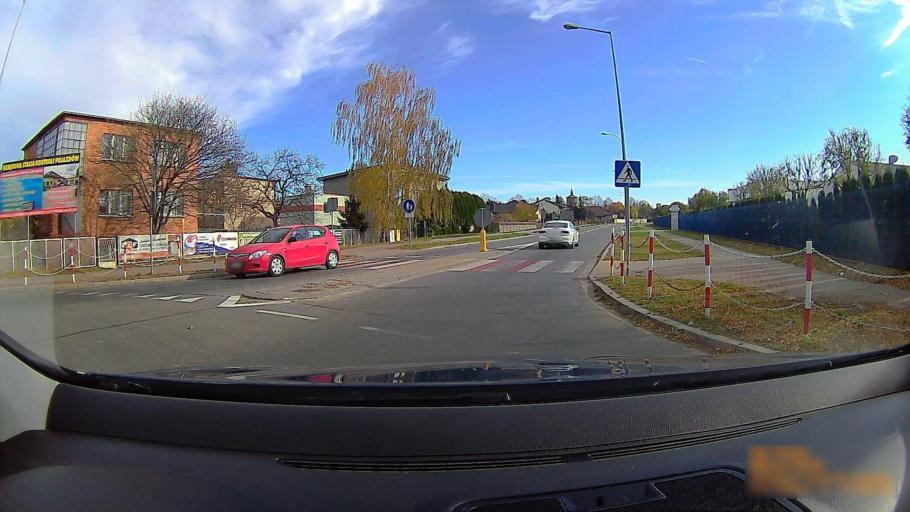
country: PL
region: Greater Poland Voivodeship
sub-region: Powiat ostrzeszowski
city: Ostrzeszow
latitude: 51.4293
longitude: 17.9350
